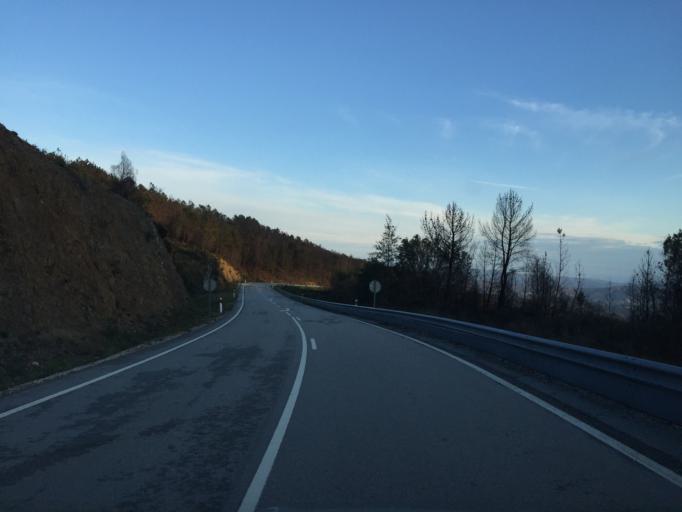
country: PT
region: Coimbra
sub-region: Pampilhosa da Serra
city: Pampilhosa da Serra
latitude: 40.1056
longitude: -7.9996
